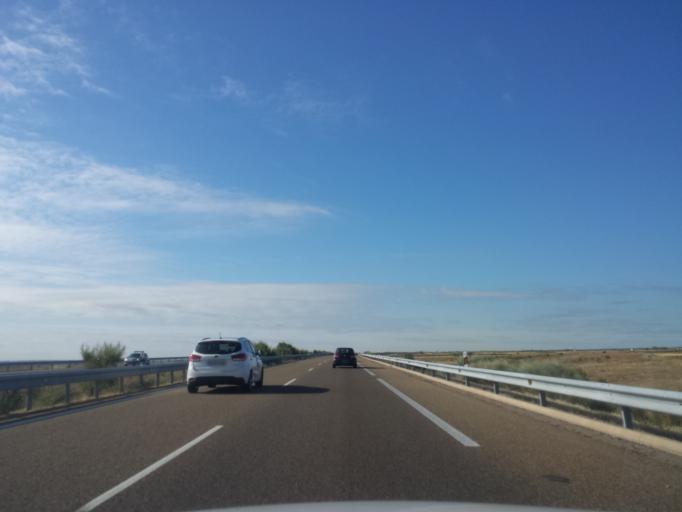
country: ES
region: Castille and Leon
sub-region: Provincia de Leon
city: Valdevimbre
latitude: 42.3763
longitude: -5.5948
